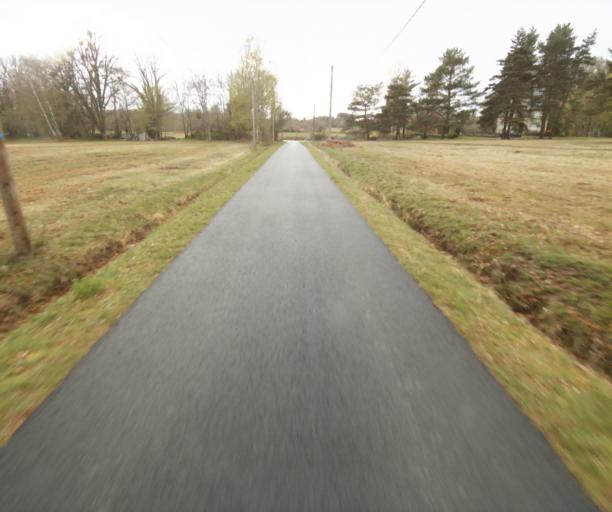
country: FR
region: Limousin
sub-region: Departement de la Correze
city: Saint-Privat
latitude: 45.2192
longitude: 2.0202
